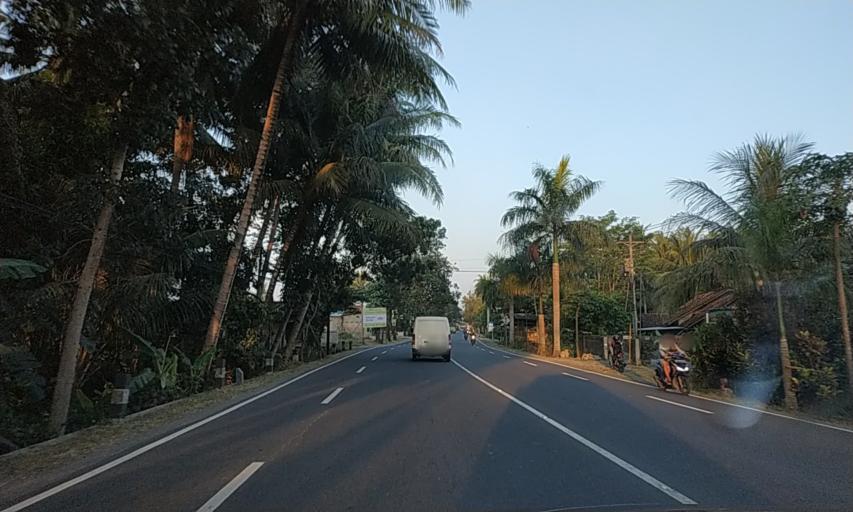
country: ID
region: Daerah Istimewa Yogyakarta
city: Srandakan
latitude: -7.8873
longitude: 110.0877
